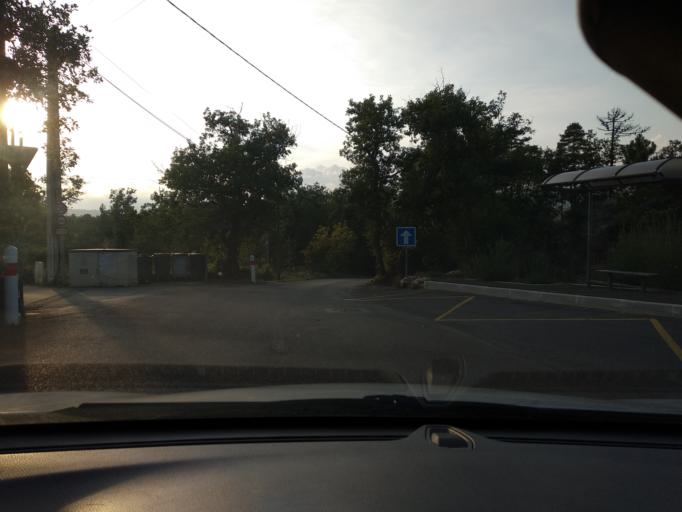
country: FR
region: Provence-Alpes-Cote d'Azur
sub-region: Departement des Alpes-Maritimes
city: Saint-Cezaire-sur-Siagne
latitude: 43.6523
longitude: 6.8135
